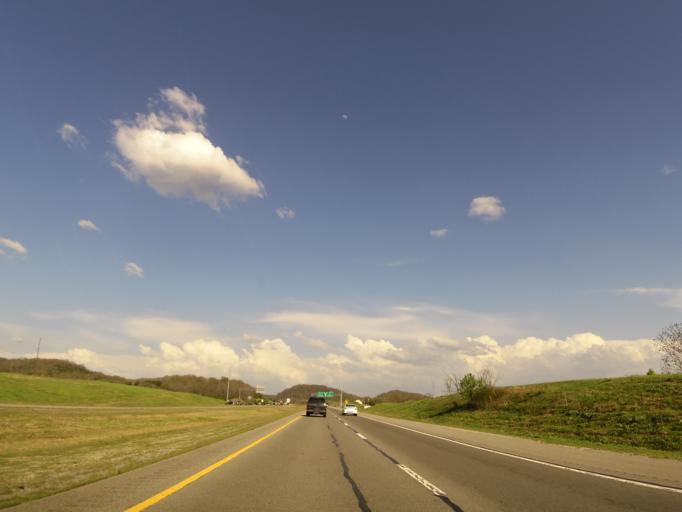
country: US
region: Tennessee
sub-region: Williamson County
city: Thompson's Station
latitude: 35.8217
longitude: -86.8555
